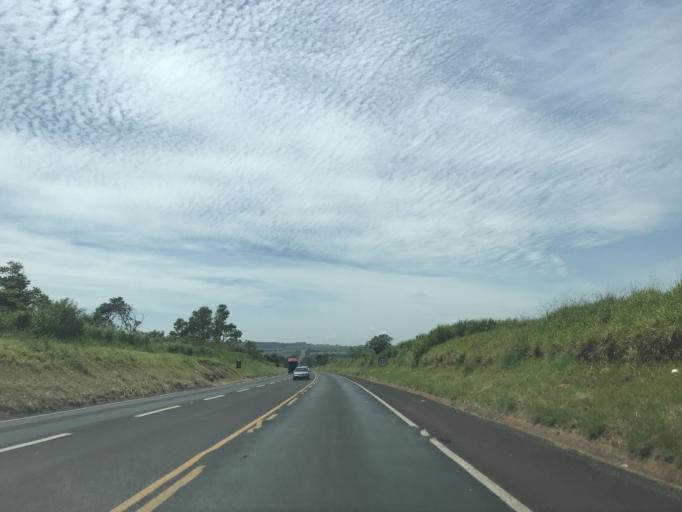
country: BR
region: Parana
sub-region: Paranavai
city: Nova Aurora
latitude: -22.9946
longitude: -52.5876
